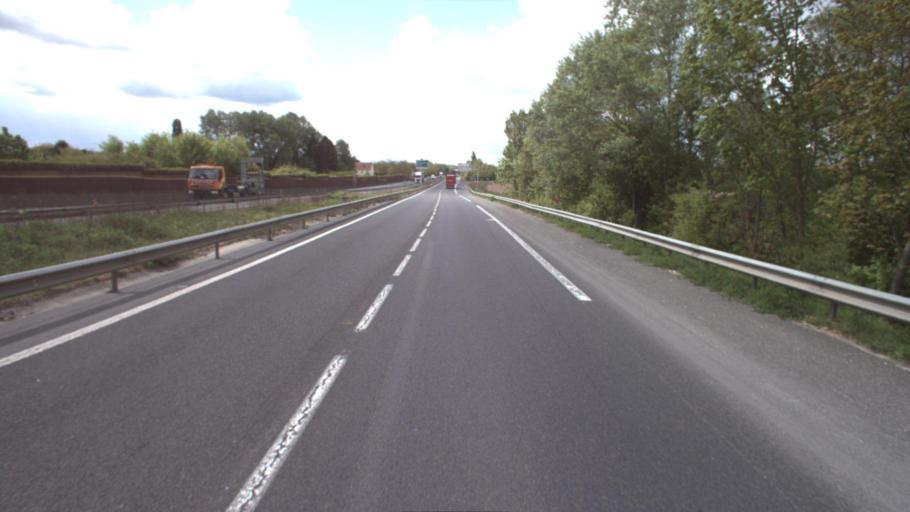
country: FR
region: Ile-de-France
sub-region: Departement de Seine-et-Marne
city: Fontenay-Tresigny
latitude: 48.7126
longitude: 2.8685
